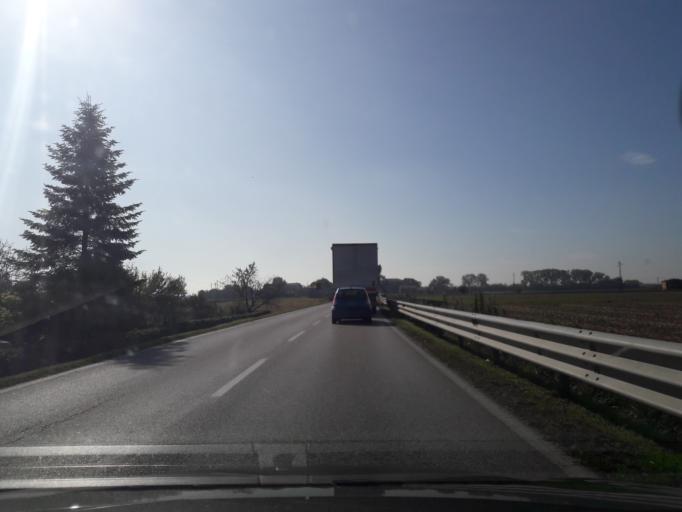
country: IT
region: Veneto
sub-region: Provincia di Rovigo
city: Adria
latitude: 45.0864
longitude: 12.0585
